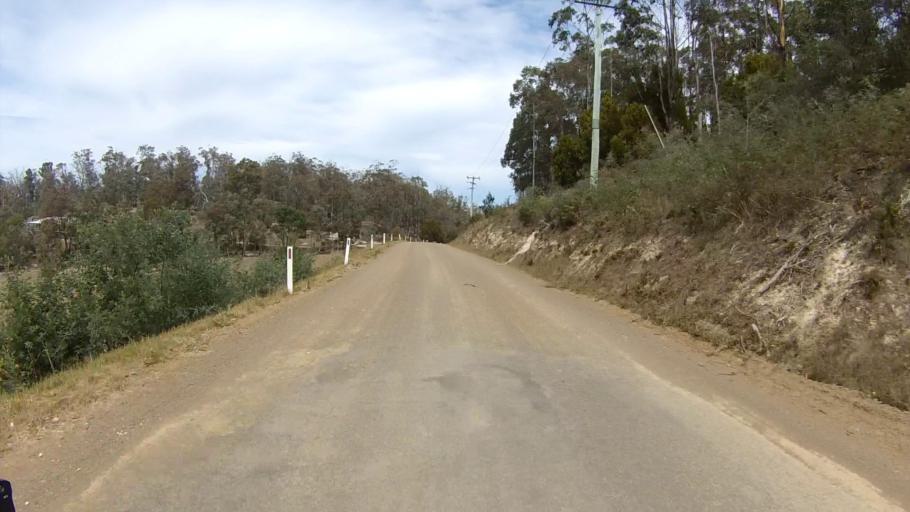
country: AU
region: Tasmania
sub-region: Sorell
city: Sorell
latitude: -42.7981
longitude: 147.6828
